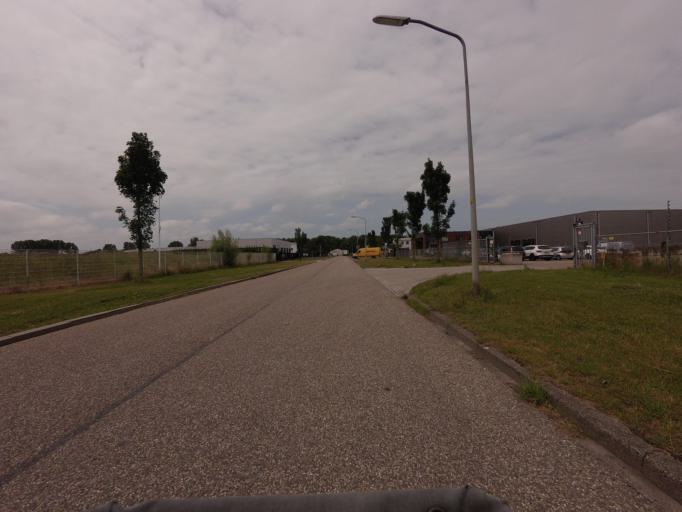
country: NL
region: Flevoland
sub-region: Gemeente Zeewolde
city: Zeewolde
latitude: 52.3556
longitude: 5.5025
